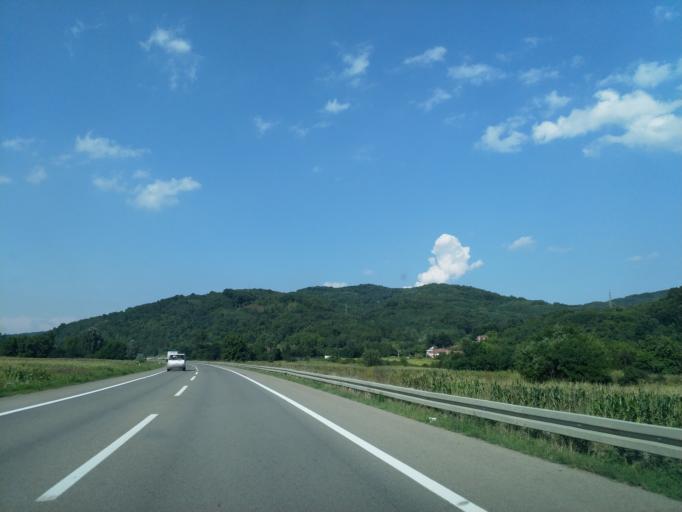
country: RS
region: Central Serbia
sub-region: Rasinski Okrug
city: Krusevac
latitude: 43.6215
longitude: 21.3715
